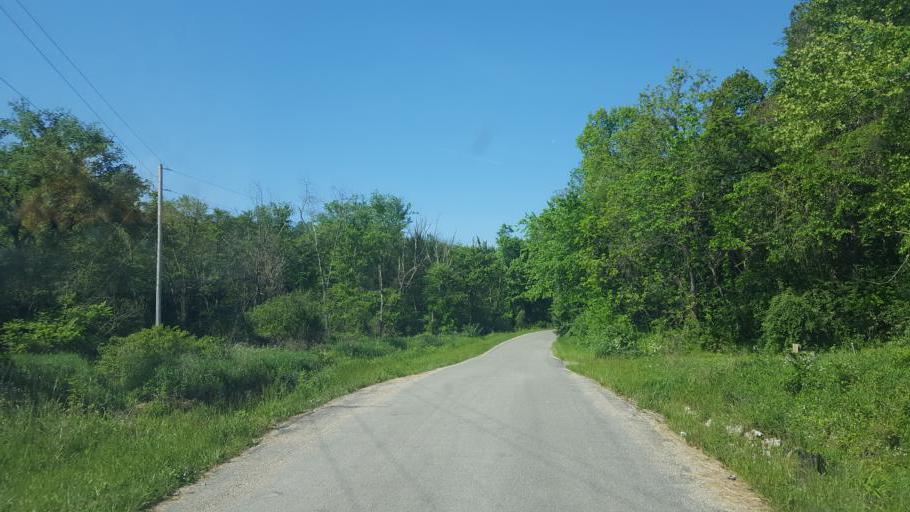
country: US
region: Ohio
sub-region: Jackson County
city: Wellston
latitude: 39.0035
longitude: -82.4749
